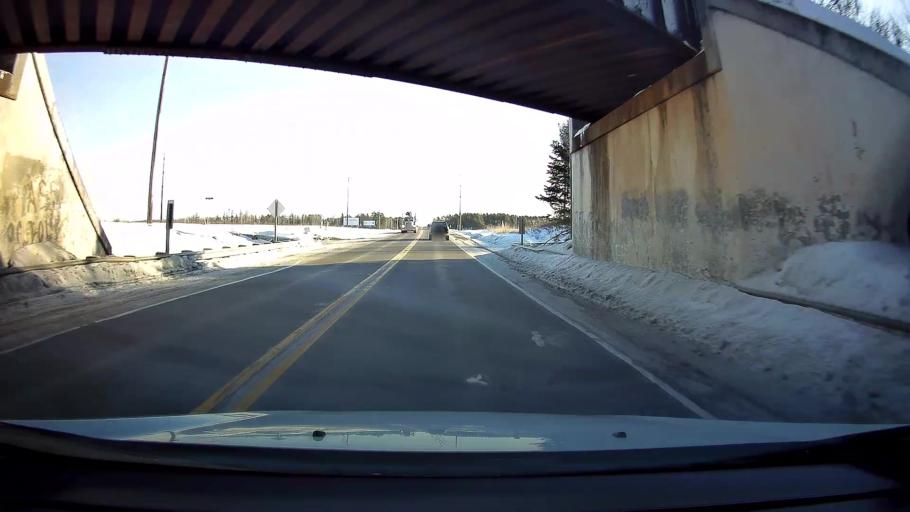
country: US
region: Wisconsin
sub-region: Sawyer County
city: Hayward
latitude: 45.9975
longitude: -91.6161
